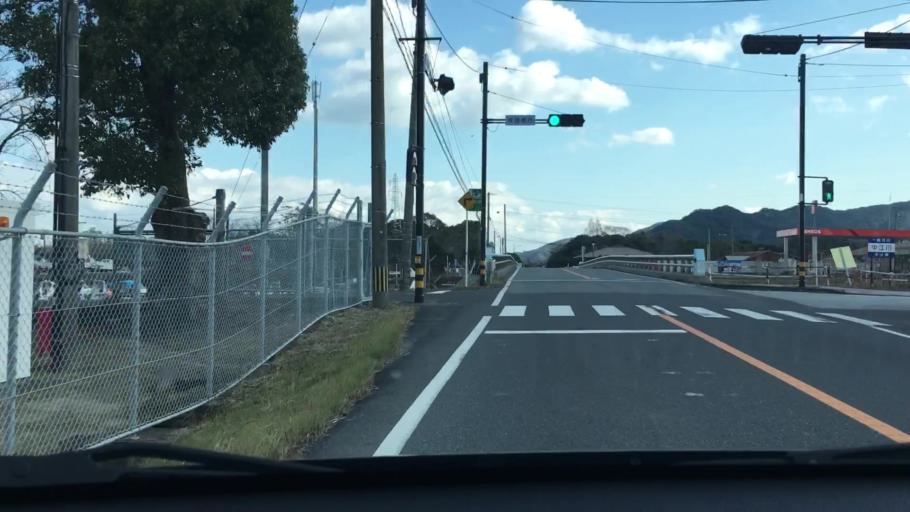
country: JP
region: Oita
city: Saiki
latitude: 32.9691
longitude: 131.9147
